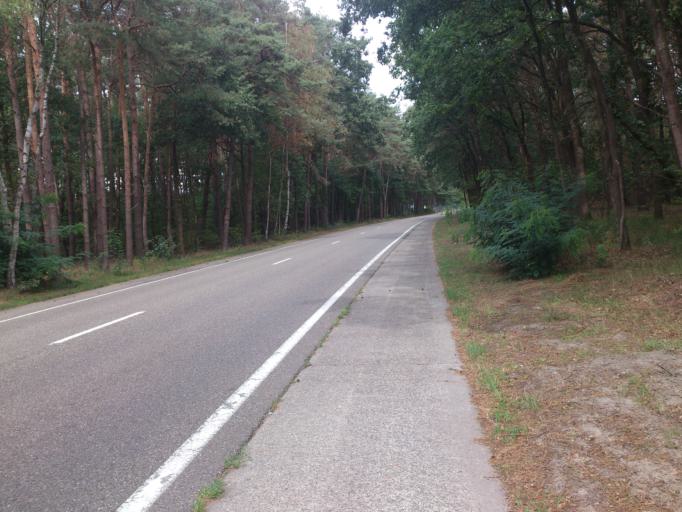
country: BE
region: Flanders
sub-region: Provincie Antwerpen
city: Mol
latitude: 51.2123
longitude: 5.1009
